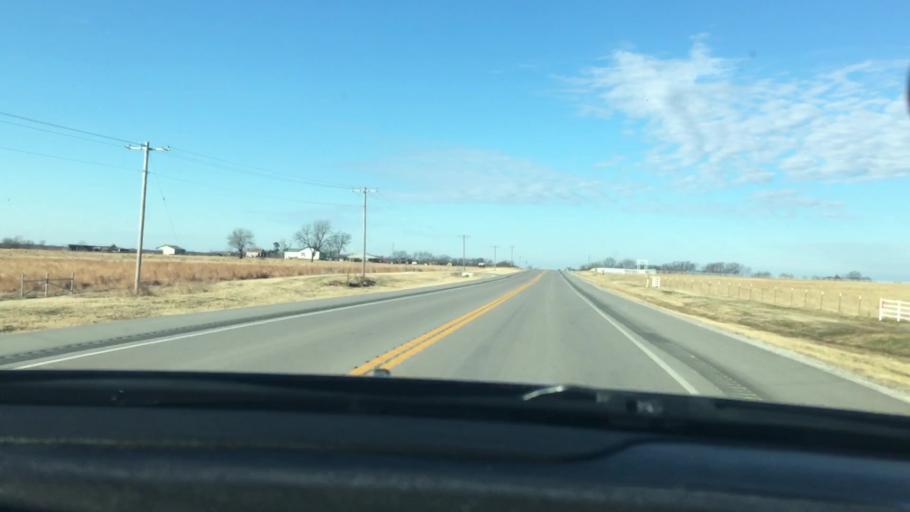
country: US
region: Oklahoma
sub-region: Love County
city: Marietta
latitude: 33.9404
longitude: -97.1897
